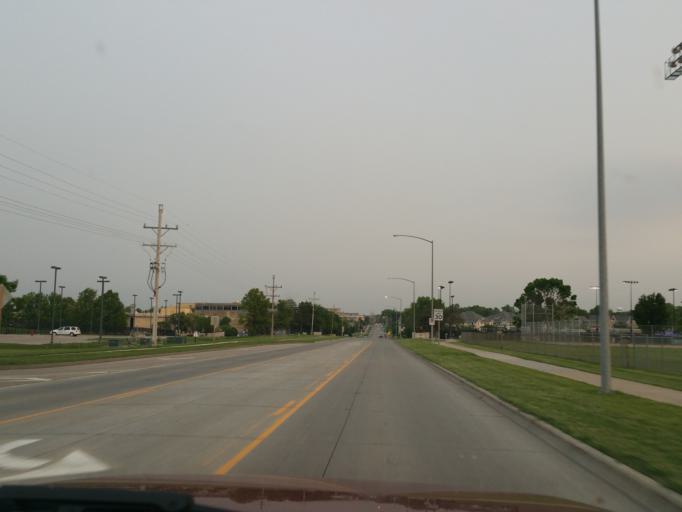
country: US
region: Kansas
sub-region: Riley County
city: Manhattan
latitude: 39.2025
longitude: -96.5852
